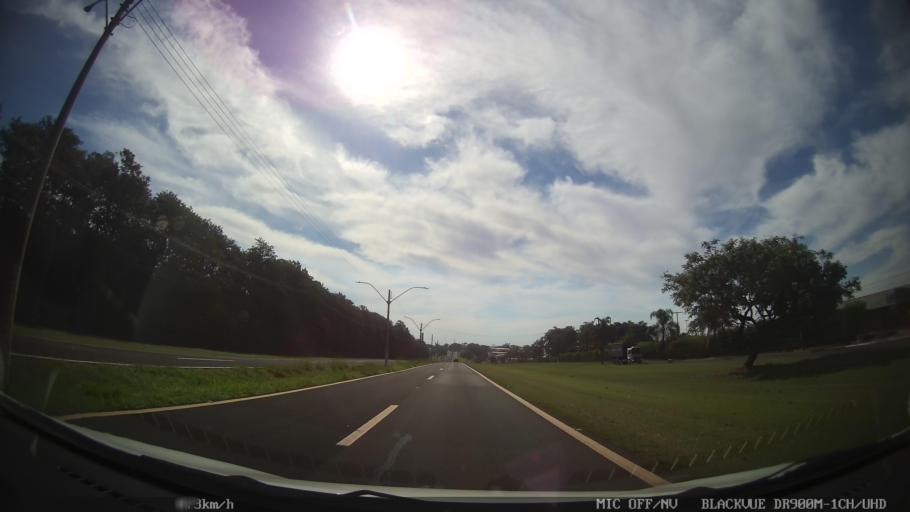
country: BR
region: Sao Paulo
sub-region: Araraquara
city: Araraquara
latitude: -21.8265
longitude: -48.1547
